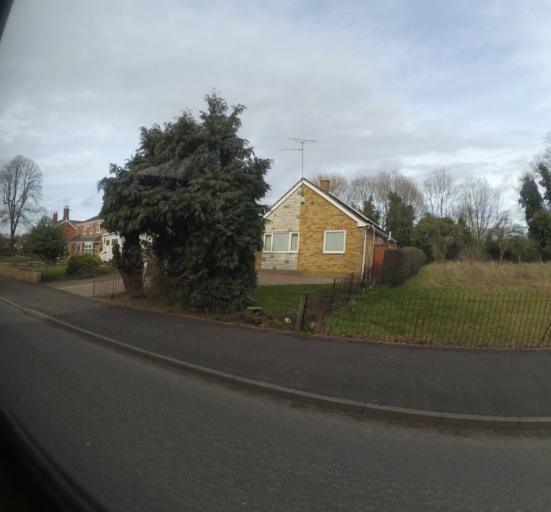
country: GB
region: England
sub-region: Warwickshire
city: Rugby
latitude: 52.3881
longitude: -1.2776
